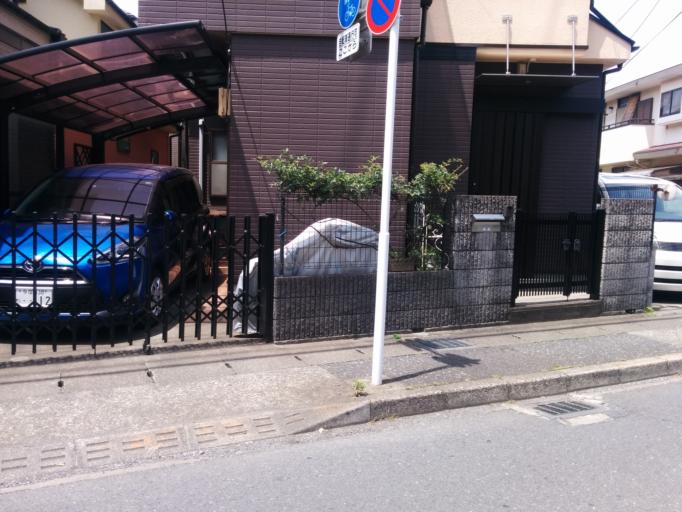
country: JP
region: Tokyo
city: Higashimurayama-shi
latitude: 35.7546
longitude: 139.4810
